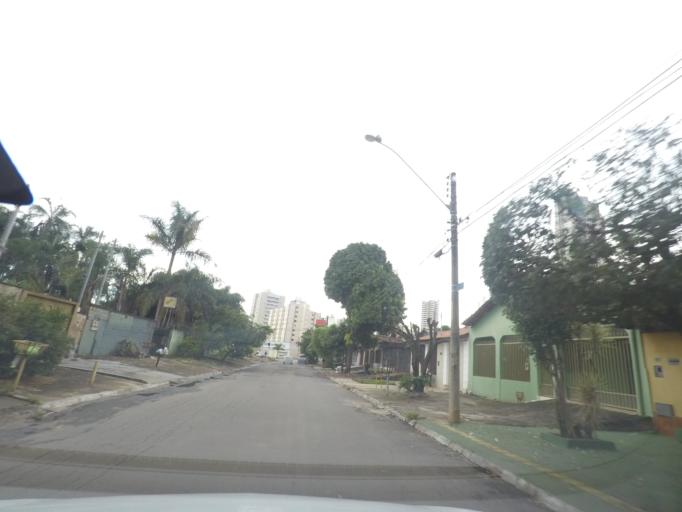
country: BR
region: Goias
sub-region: Goiania
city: Goiania
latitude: -16.7149
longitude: -49.2438
